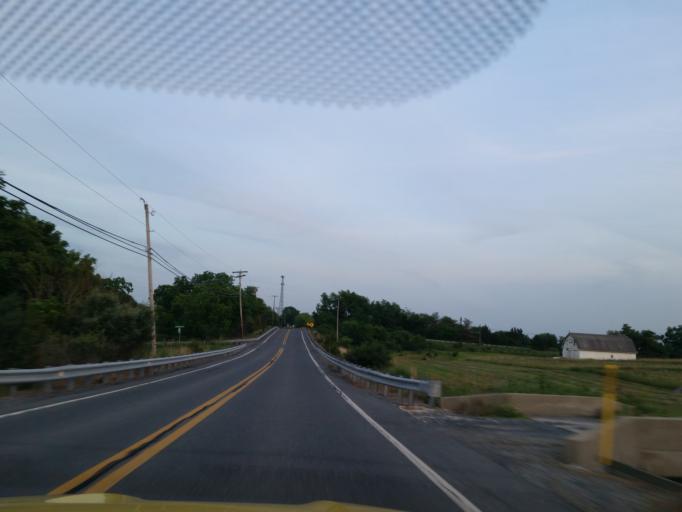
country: US
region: Pennsylvania
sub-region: Lebanon County
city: Palmyra
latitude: 40.4092
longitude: -76.6024
